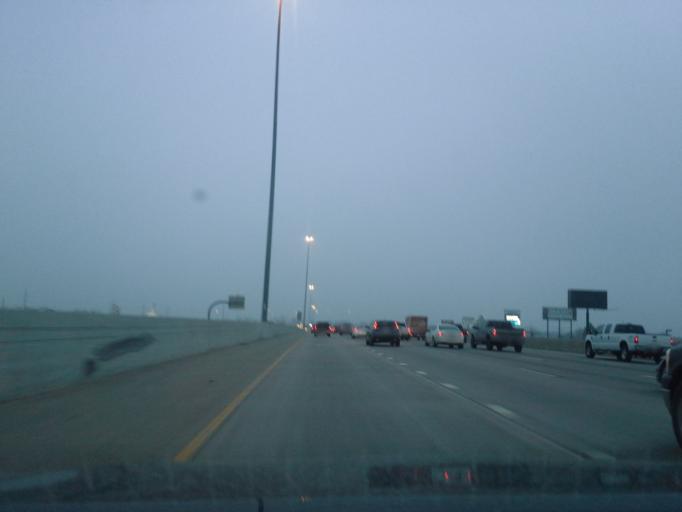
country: US
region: Utah
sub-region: Salt Lake County
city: Murray
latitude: 40.6537
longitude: -111.9019
